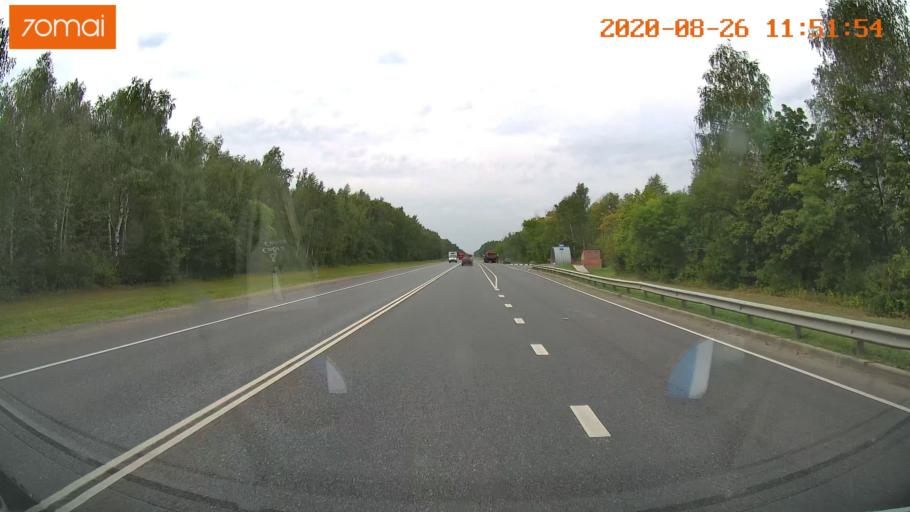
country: RU
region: Rjazan
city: Lesnoy
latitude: 54.2959
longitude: 40.4682
